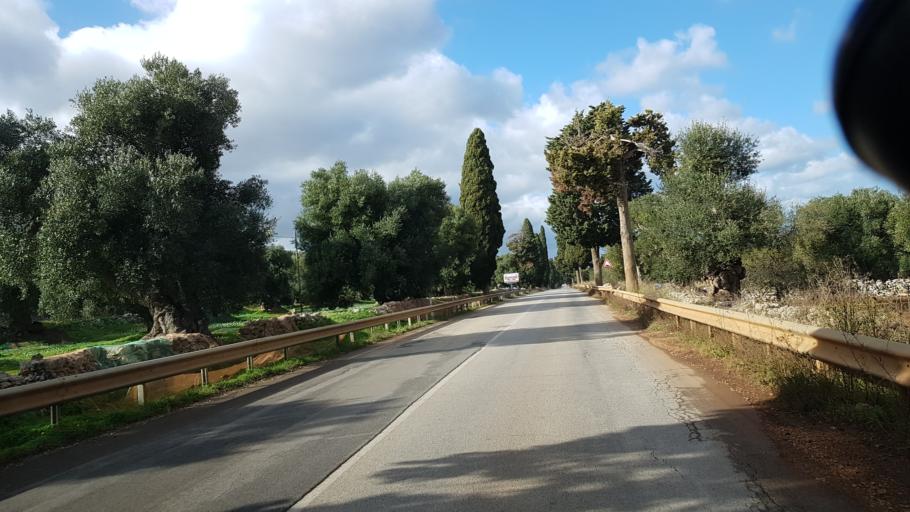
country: IT
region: Apulia
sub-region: Provincia di Brindisi
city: Ostuni
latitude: 40.7516
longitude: 17.5486
